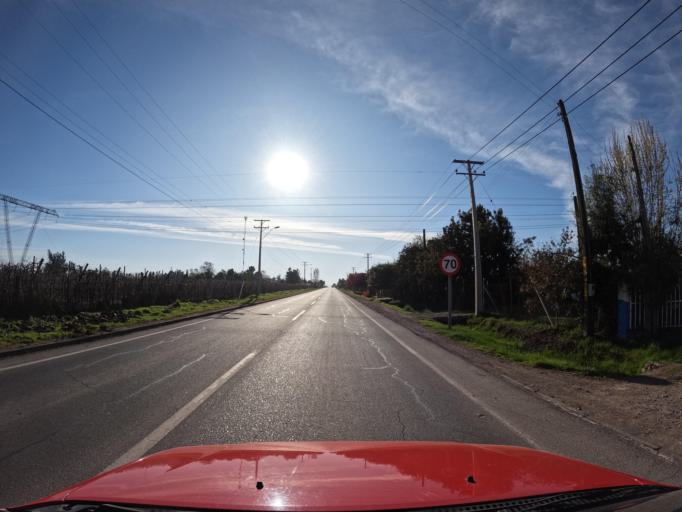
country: CL
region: Maule
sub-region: Provincia de Curico
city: Teno
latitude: -34.9506
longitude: -70.9869
